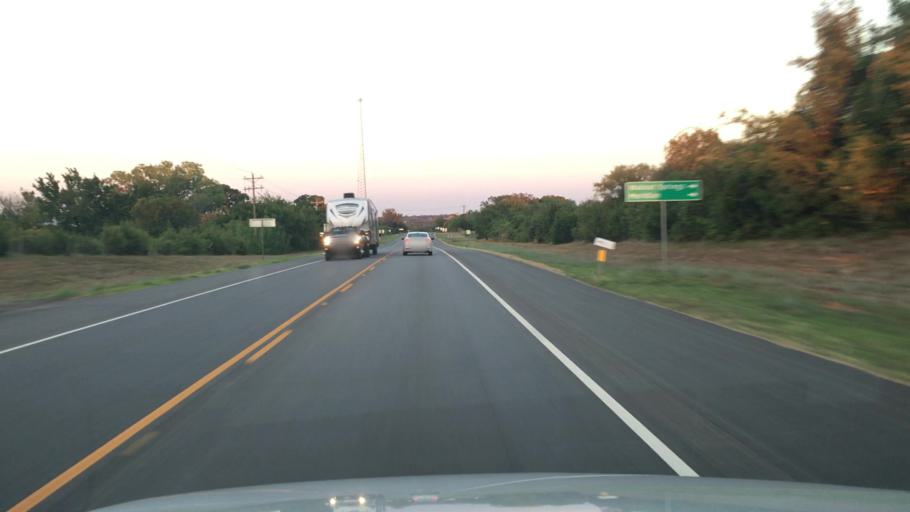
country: US
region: Texas
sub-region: Somervell County
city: Glen Rose
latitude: 32.1920
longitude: -97.8397
